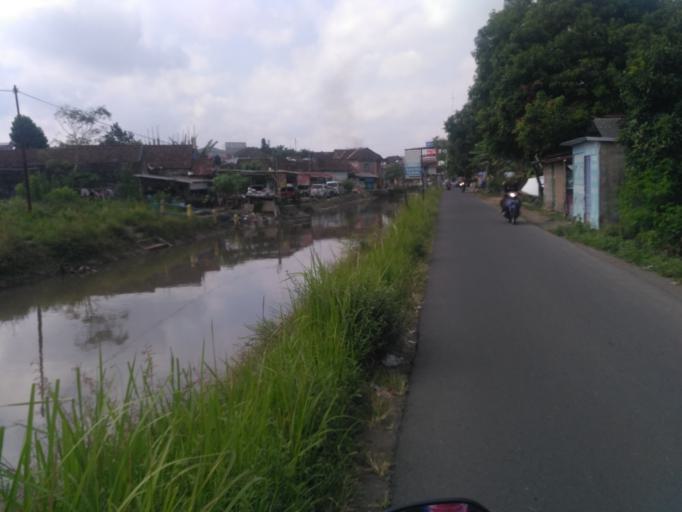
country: ID
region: Daerah Istimewa Yogyakarta
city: Yogyakarta
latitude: -7.7601
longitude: 110.3600
